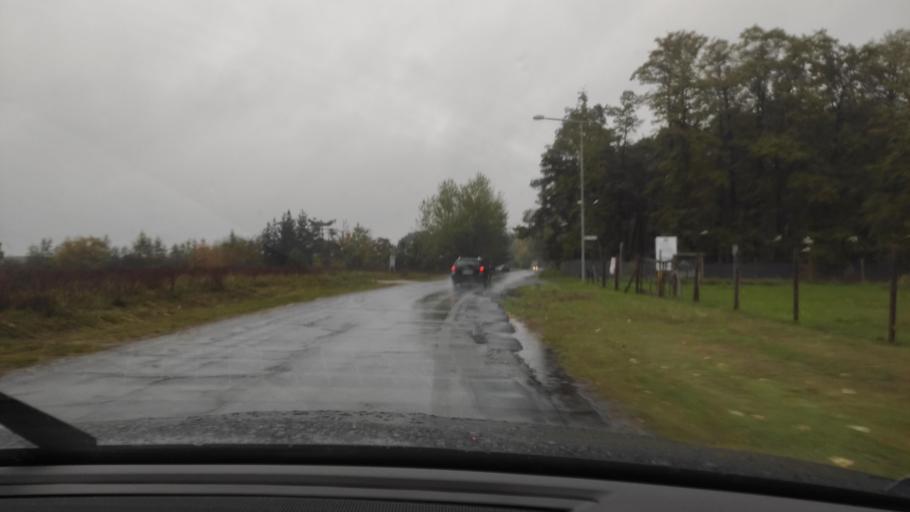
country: PL
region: Greater Poland Voivodeship
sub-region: Powiat poznanski
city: Kornik
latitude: 52.2162
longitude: 17.0982
